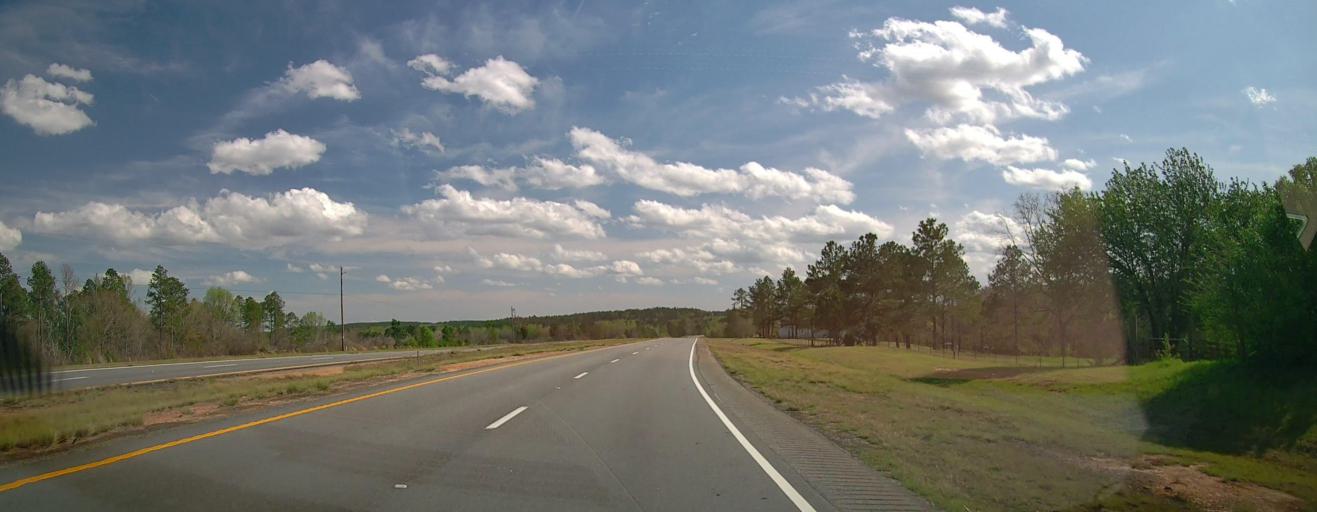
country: US
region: Georgia
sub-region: Baldwin County
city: Hardwick
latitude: 32.9944
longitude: -83.2134
